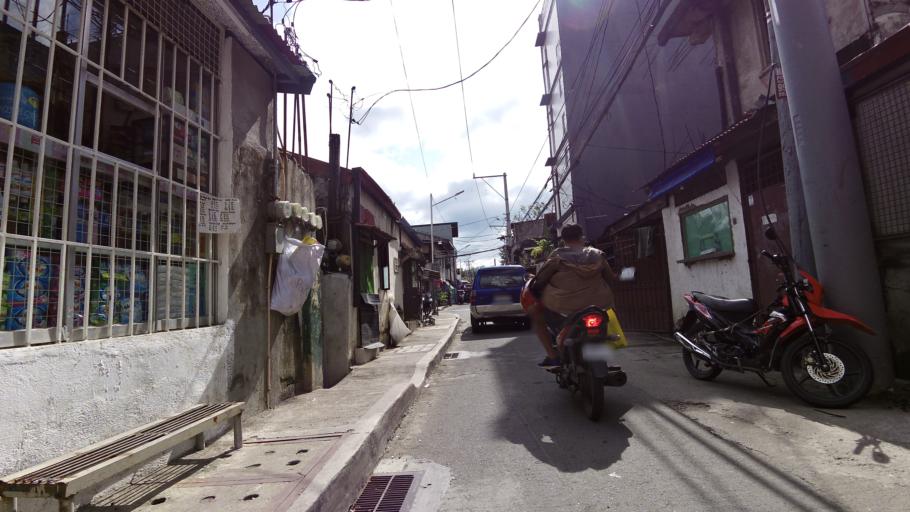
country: PH
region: Calabarzon
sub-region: Province of Rizal
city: Cainta
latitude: 14.5745
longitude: 121.1184
